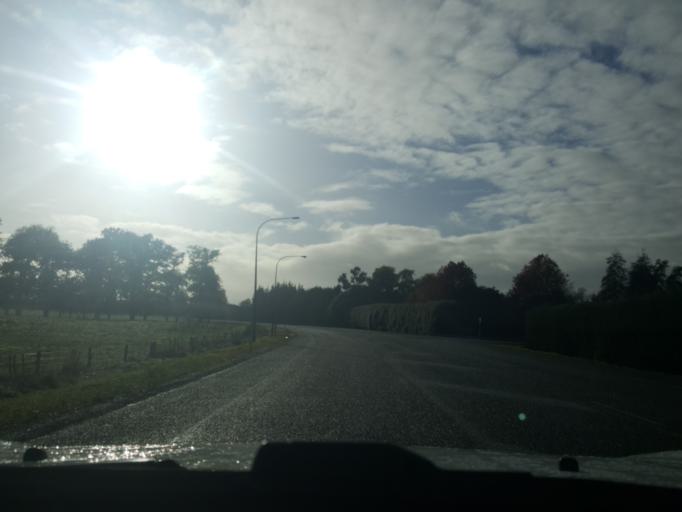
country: NZ
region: Waikato
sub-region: Waipa District
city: Cambridge
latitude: -37.7791
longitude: 175.4002
